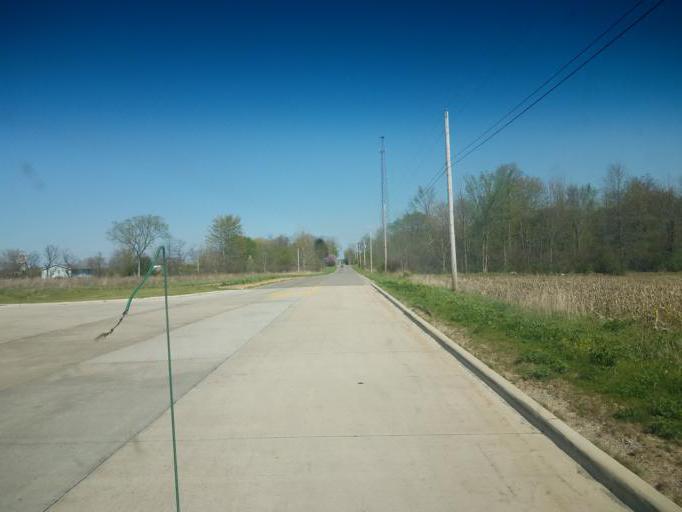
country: US
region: Ohio
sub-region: Medina County
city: Lodi
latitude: 40.9958
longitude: -81.9914
